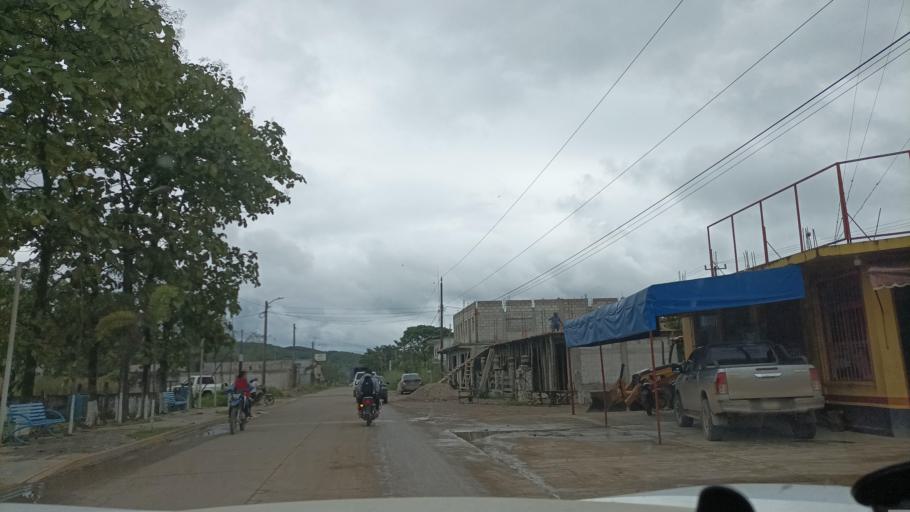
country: MX
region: Veracruz
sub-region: Uxpanapa
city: Poblado 10
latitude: 17.2794
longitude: -94.4553
